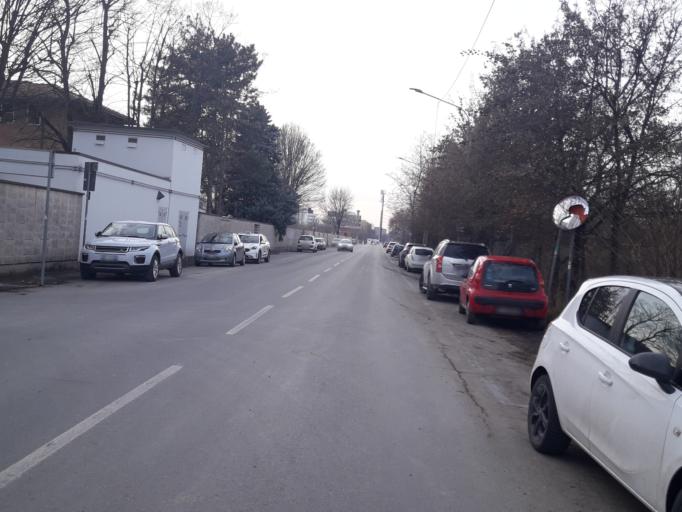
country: IT
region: Emilia-Romagna
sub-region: Provincia di Bologna
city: Bologna
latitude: 44.5068
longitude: 11.3147
